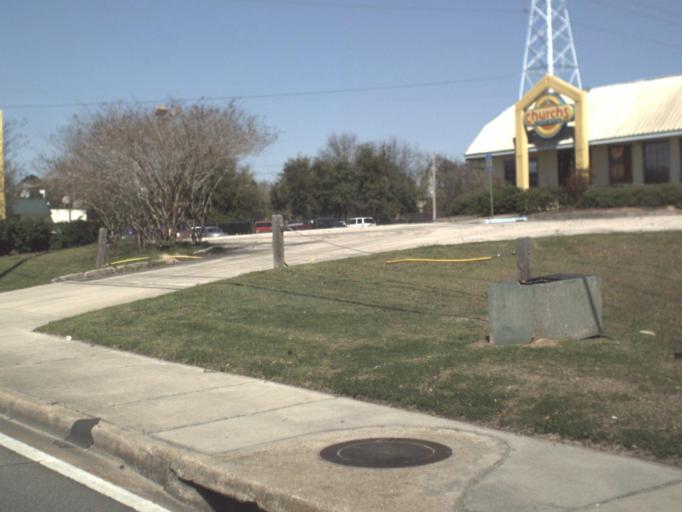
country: US
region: Florida
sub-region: Leon County
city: Tallahassee
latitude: 30.4314
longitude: -84.3022
